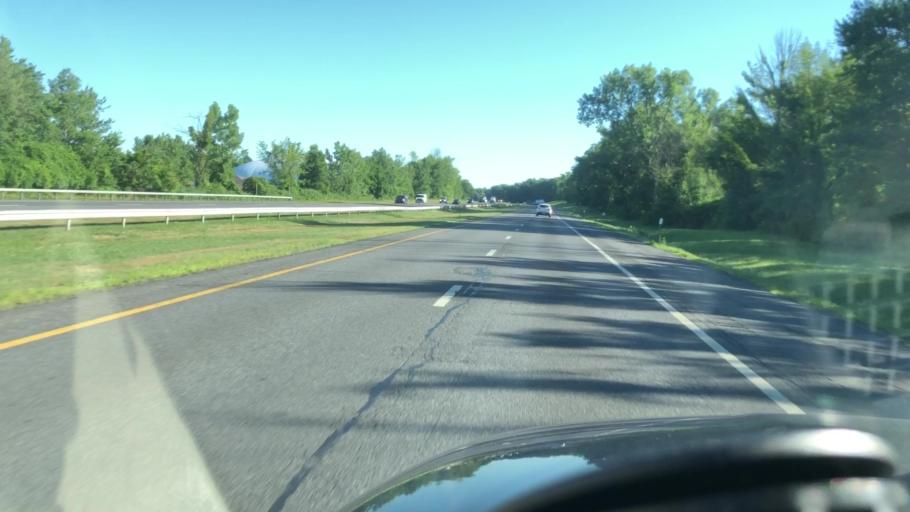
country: US
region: New York
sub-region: Albany County
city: Delmar
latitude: 42.5781
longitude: -73.7877
